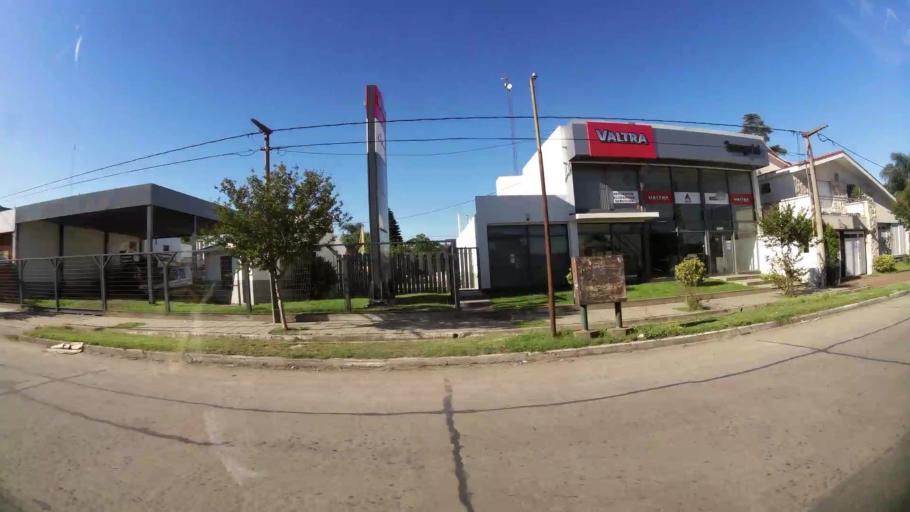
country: AR
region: Cordoba
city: San Francisco
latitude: -31.4160
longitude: -62.0871
